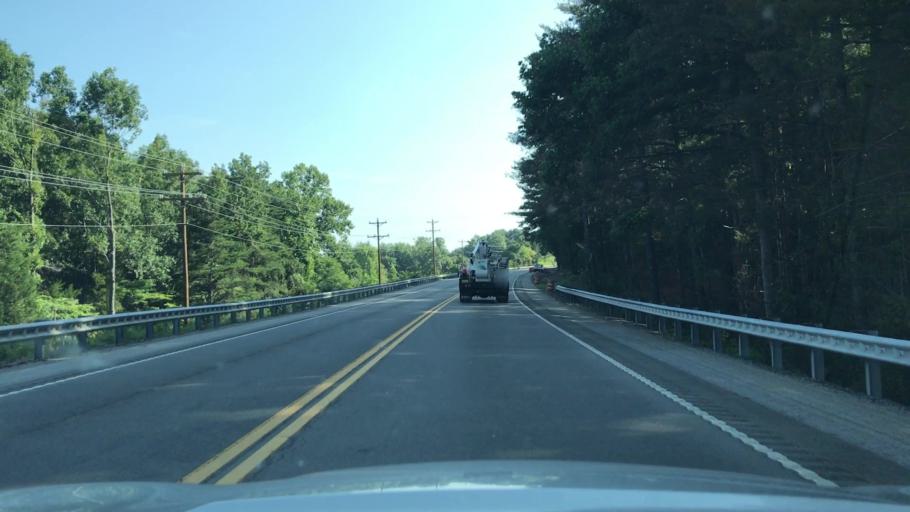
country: US
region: Tennessee
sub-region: Overton County
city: Livingston
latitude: 36.4316
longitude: -85.2792
